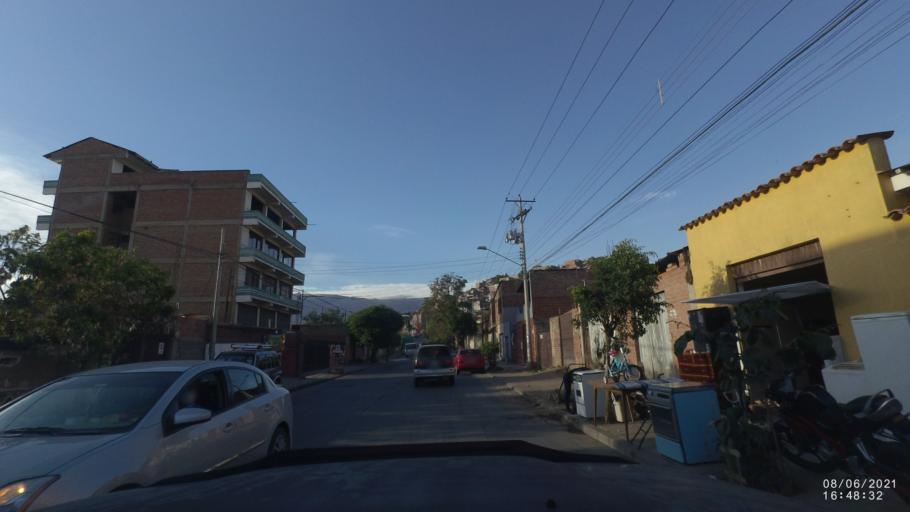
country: BO
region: Cochabamba
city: Cochabamba
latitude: -17.4196
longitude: -66.1511
